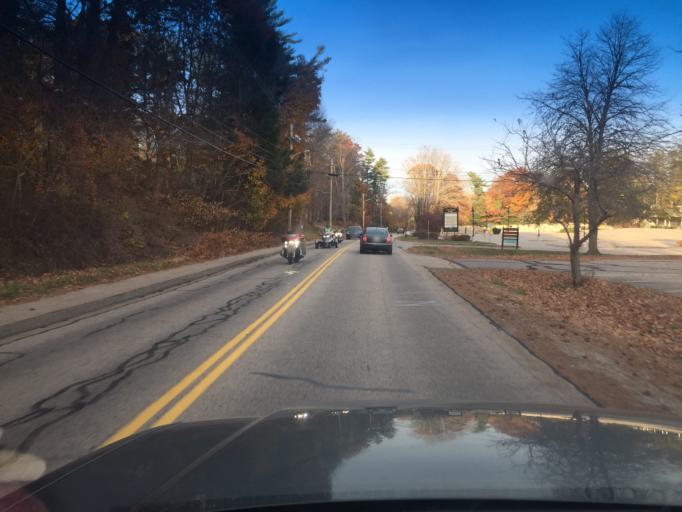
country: US
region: Maine
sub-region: York County
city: York Harbor
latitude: 43.1476
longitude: -70.6435
